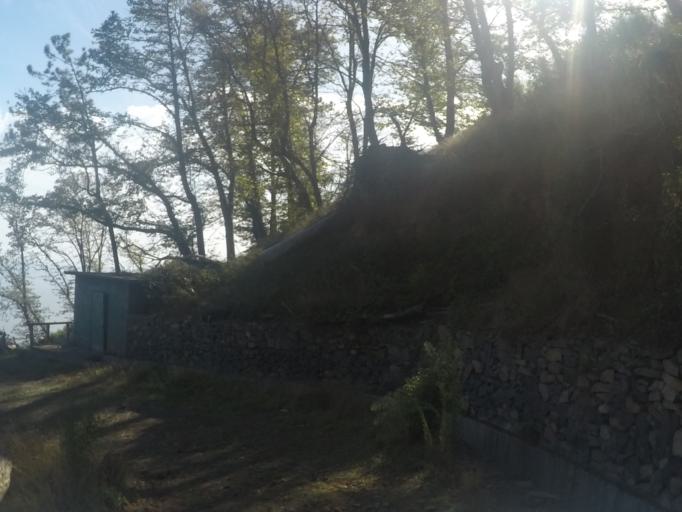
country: PT
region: Madeira
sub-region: Funchal
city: Nossa Senhora do Monte
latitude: 32.6994
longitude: -16.9138
